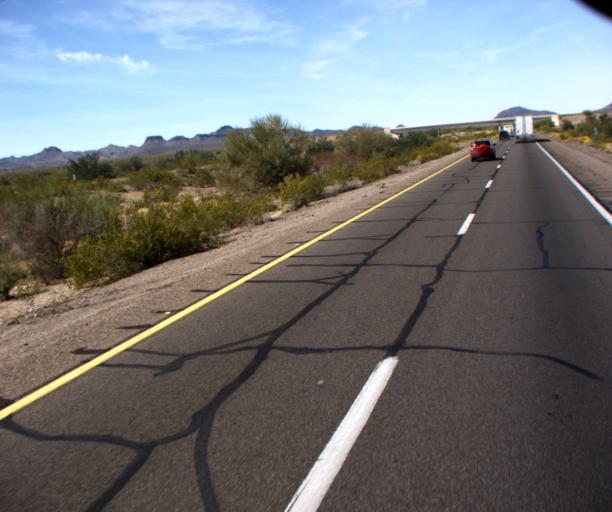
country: US
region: Arizona
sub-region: La Paz County
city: Quartzsite
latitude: 33.6561
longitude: -113.9611
